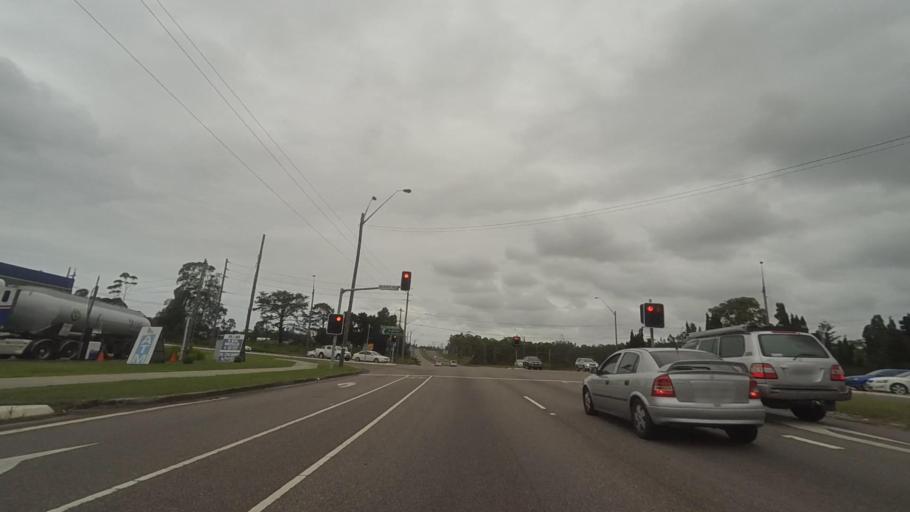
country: AU
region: New South Wales
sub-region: Wyong Shire
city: Buff Point
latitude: -33.1992
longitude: 151.5229
